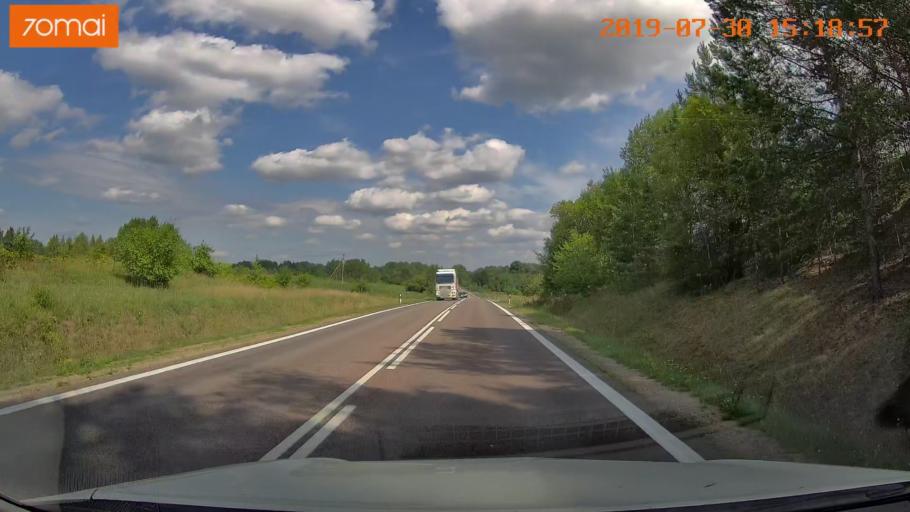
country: LT
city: Aukstadvaris
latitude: 54.5760
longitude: 24.4394
